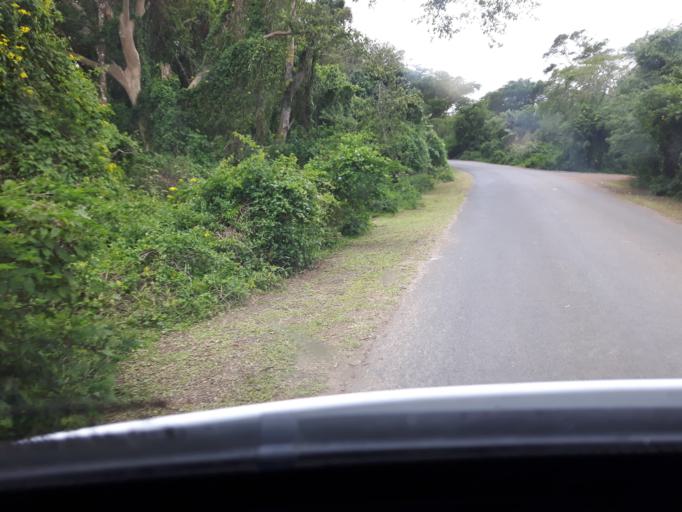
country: ZA
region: KwaZulu-Natal
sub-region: uMkhanyakude District Municipality
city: Mtubatuba
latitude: -28.3847
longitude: 32.4145
